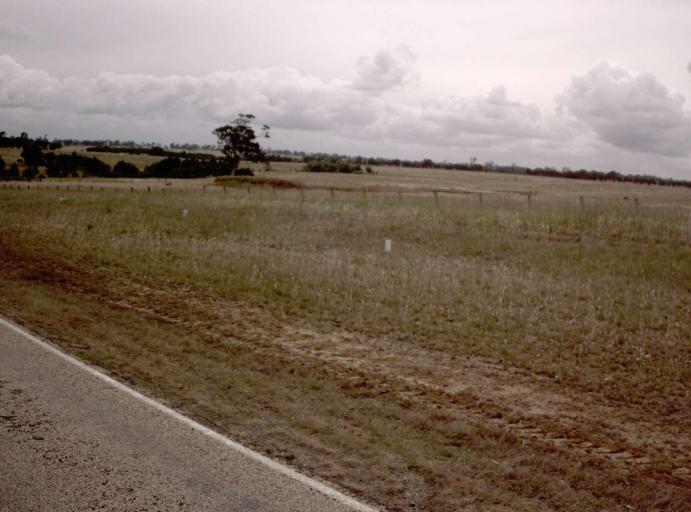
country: AU
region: Victoria
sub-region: Wellington
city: Sale
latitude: -37.9444
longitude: 147.0911
